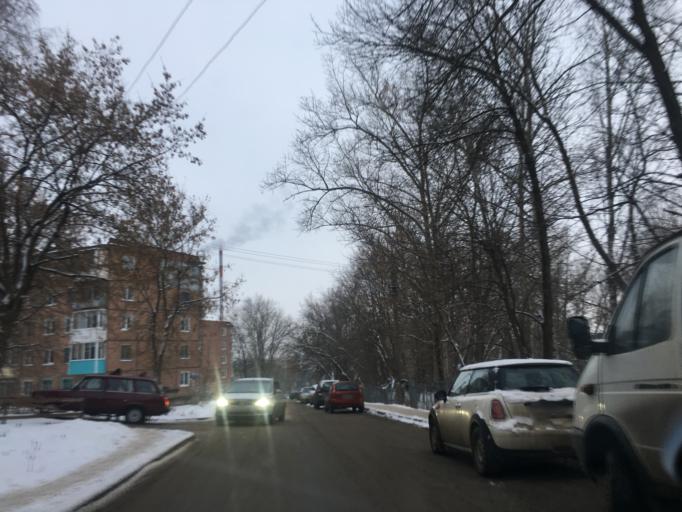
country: RU
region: Tula
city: Mendeleyevskiy
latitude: 54.1775
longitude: 37.5699
